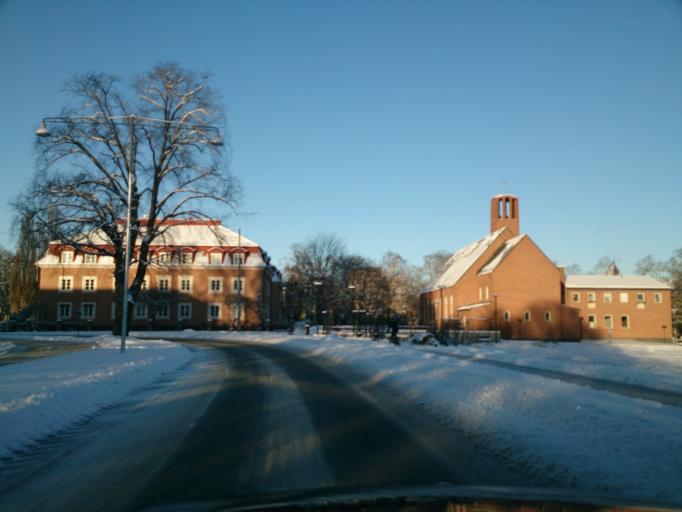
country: SE
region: OEstergoetland
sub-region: Norrkopings Kommun
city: Norrkoping
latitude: 58.5832
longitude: 16.1923
